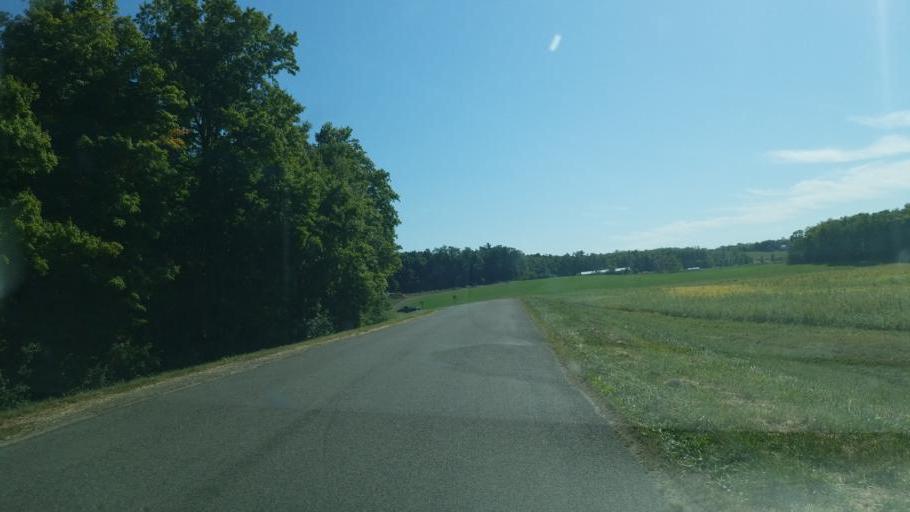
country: US
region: Ohio
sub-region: Champaign County
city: North Lewisburg
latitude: 40.1676
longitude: -83.6079
